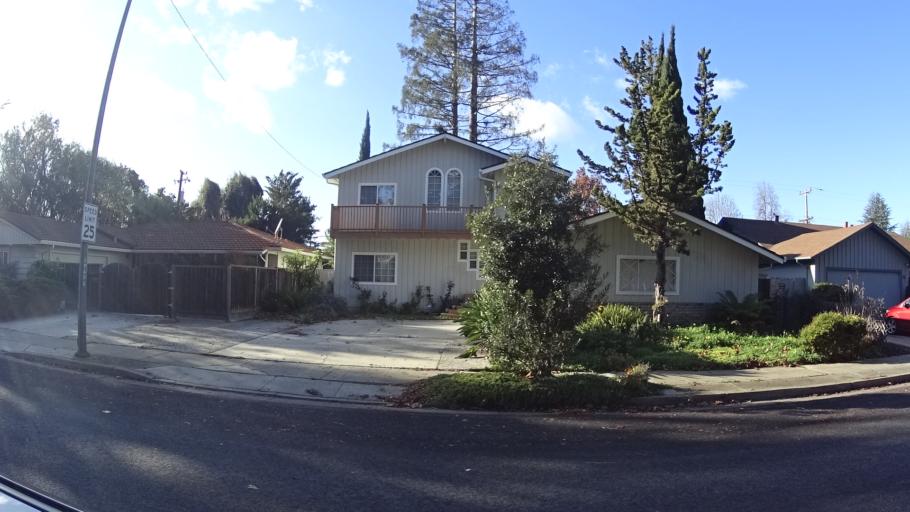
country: US
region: California
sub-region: Santa Clara County
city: Sunnyvale
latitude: 37.3777
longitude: -122.0425
